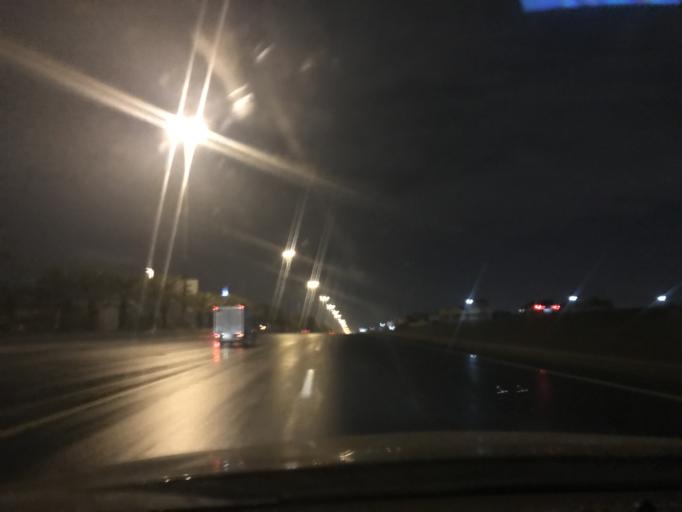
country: SA
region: Ar Riyad
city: Riyadh
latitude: 24.7388
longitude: 46.5952
